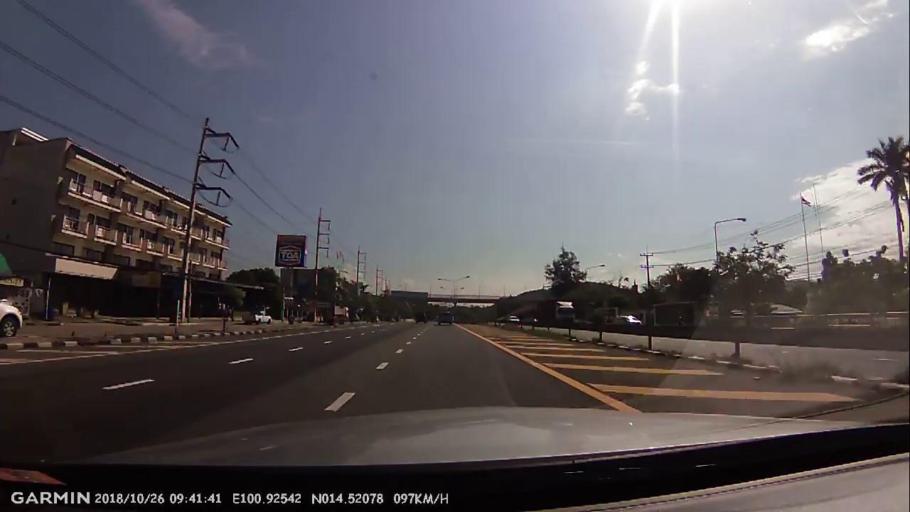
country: TH
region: Sara Buri
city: Saraburi
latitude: 14.5216
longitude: 100.9249
